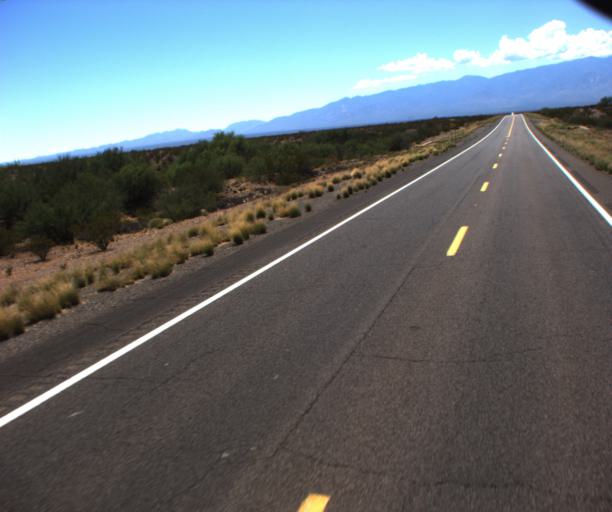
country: US
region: Arizona
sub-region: Graham County
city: Safford
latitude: 32.7987
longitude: -109.5326
